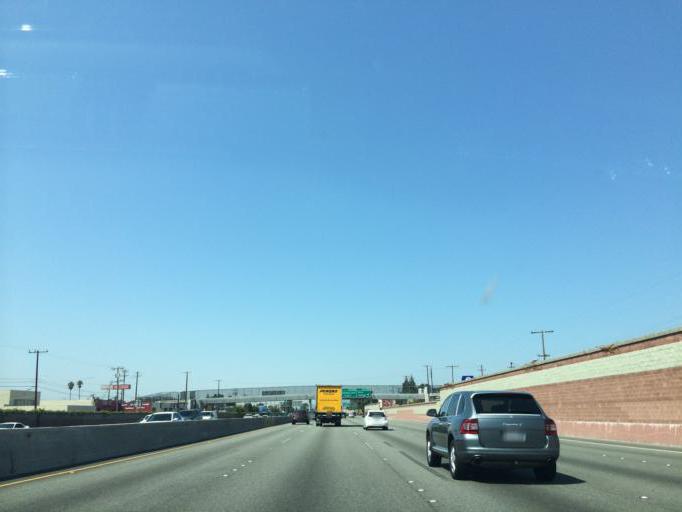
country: US
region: California
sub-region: San Mateo County
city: San Mateo
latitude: 37.5750
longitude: -122.3184
